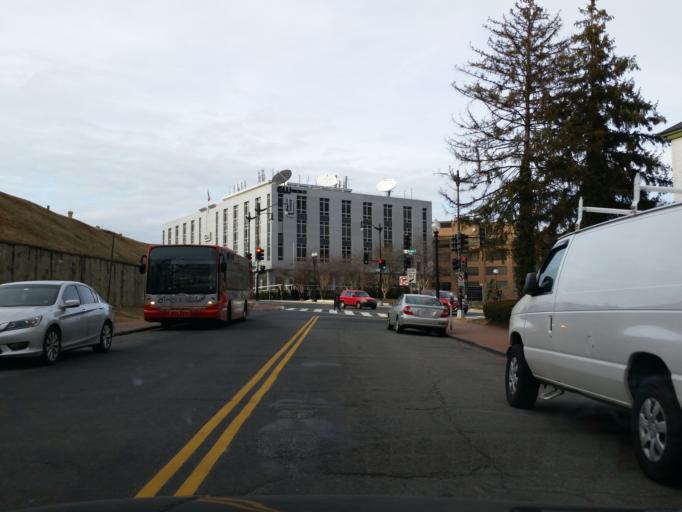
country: US
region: Washington, D.C.
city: Washington, D.C.
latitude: 38.9172
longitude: -77.0694
